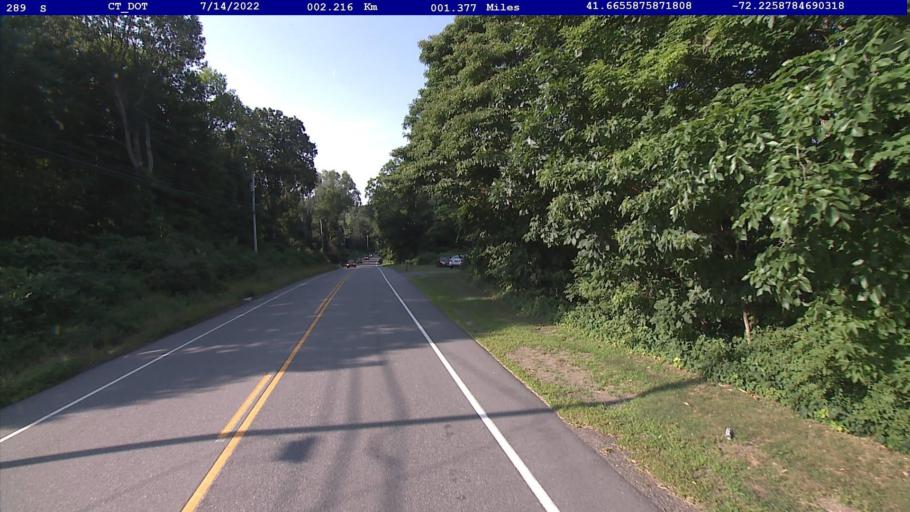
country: US
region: Connecticut
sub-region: Windham County
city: Willimantic
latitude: 41.6656
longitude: -72.2259
